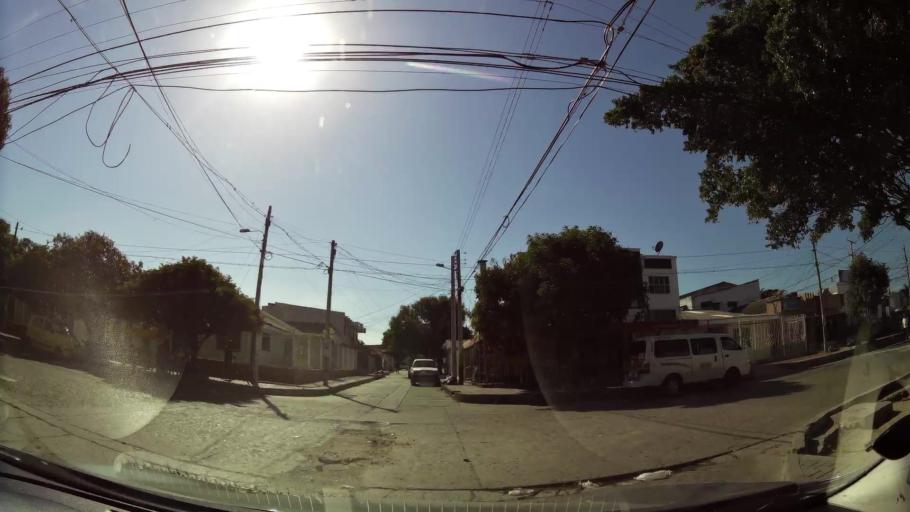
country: CO
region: Atlantico
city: Barranquilla
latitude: 10.9456
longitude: -74.7921
